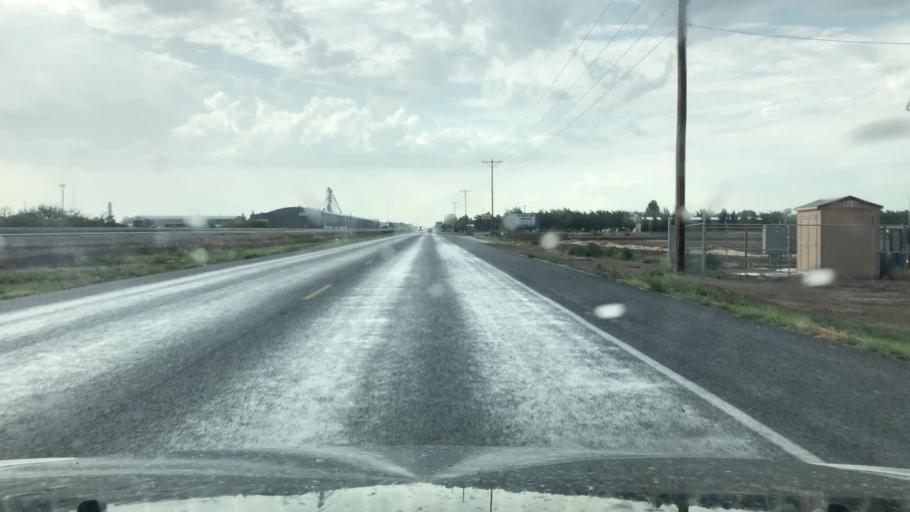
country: US
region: New Mexico
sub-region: Dona Ana County
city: Mesquite
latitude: 32.1578
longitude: -106.6923
